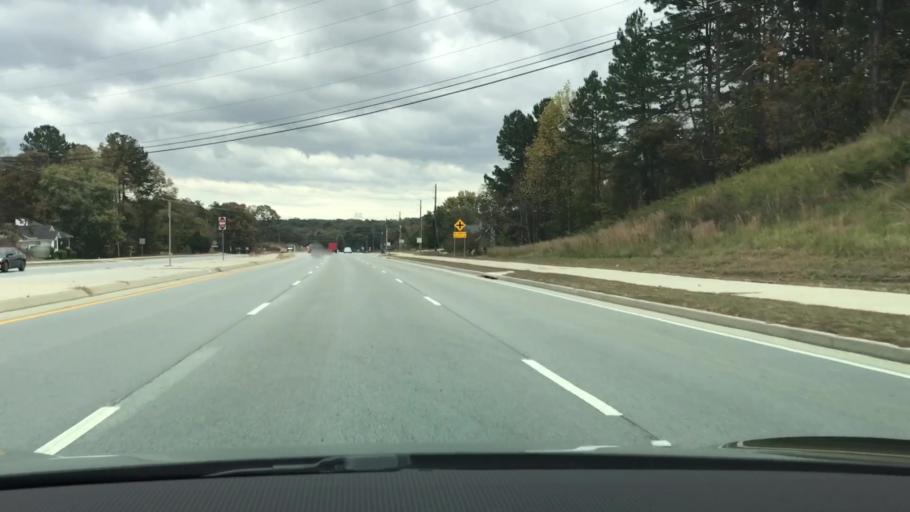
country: US
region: Georgia
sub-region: Hall County
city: Flowery Branch
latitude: 34.1150
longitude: -83.9016
